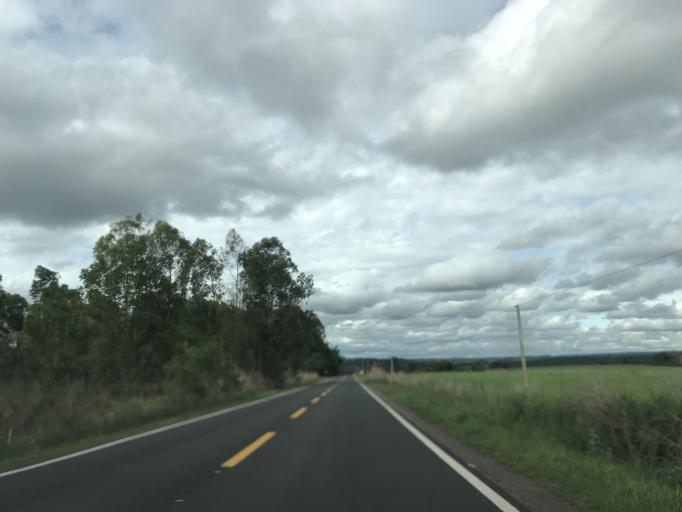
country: BR
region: Goias
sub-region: Bela Vista De Goias
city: Bela Vista de Goias
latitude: -17.1834
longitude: -48.6898
